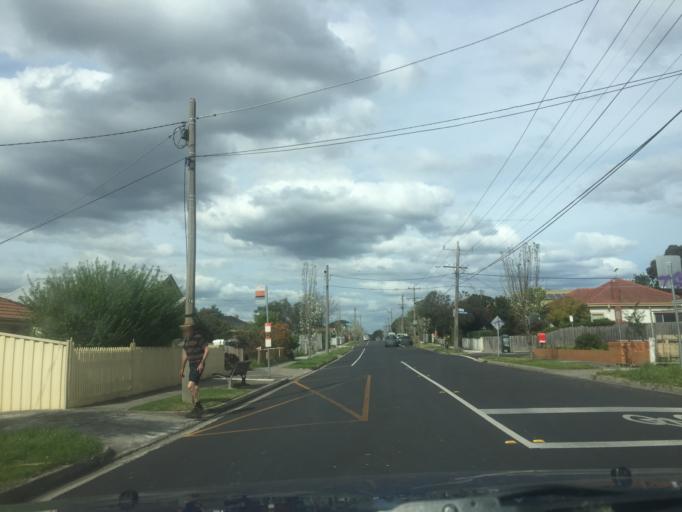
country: AU
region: Victoria
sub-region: Darebin
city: Preston
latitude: -37.7349
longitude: 145.0191
